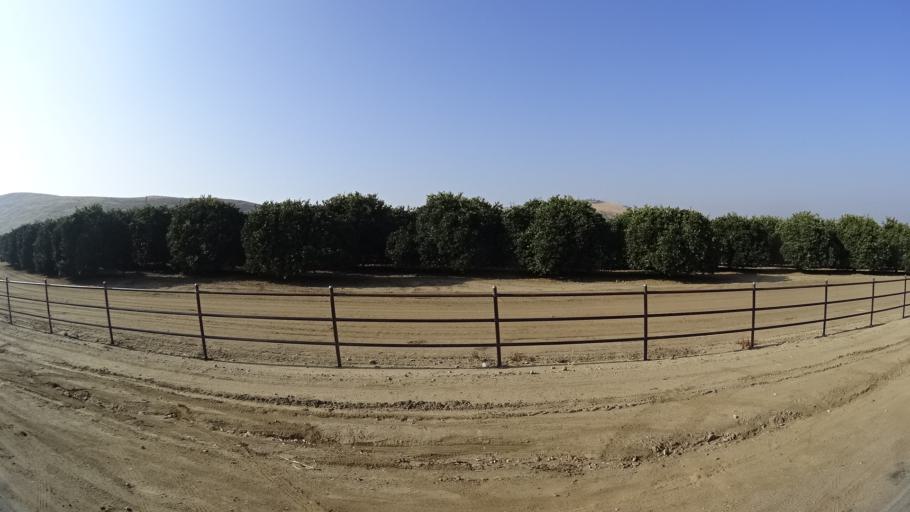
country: US
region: California
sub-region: Kern County
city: Lamont
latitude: 35.4173
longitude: -118.8318
